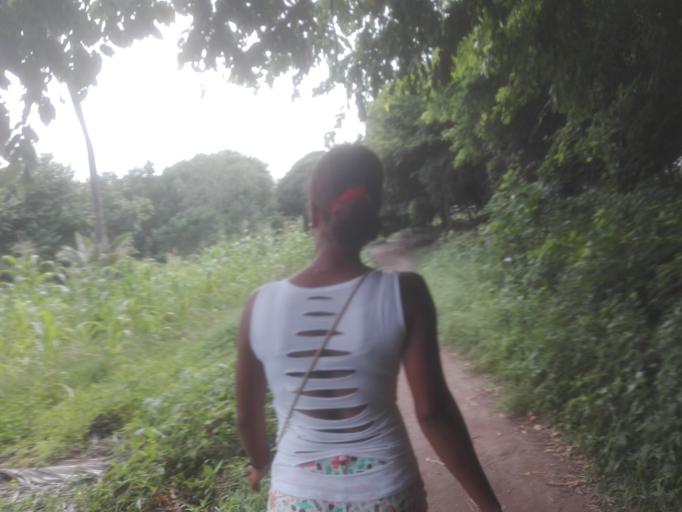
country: CO
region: Bolivar
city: Turbana
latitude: 10.1798
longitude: -75.7358
